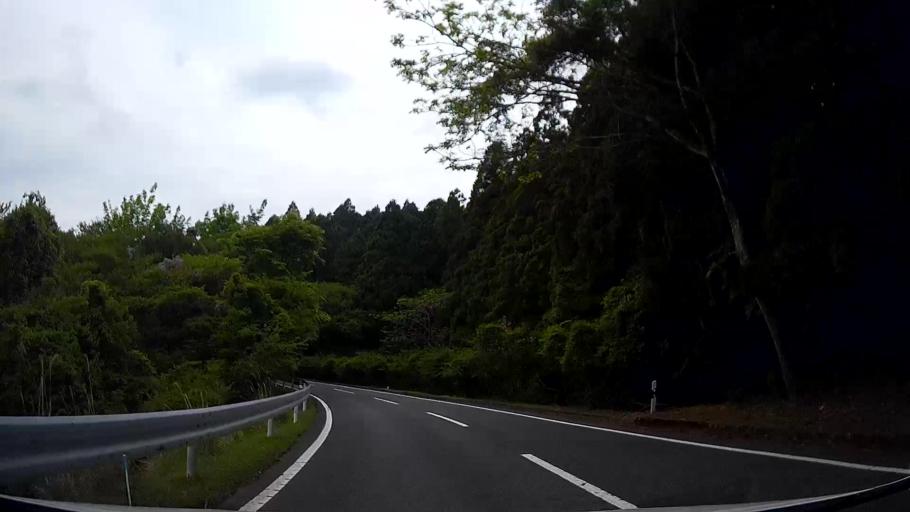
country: JP
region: Shizuoka
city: Ito
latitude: 34.9078
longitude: 139.0555
